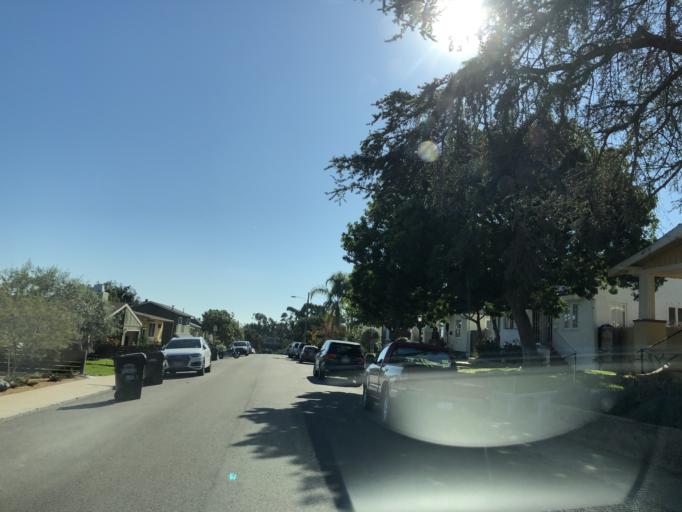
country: US
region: California
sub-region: San Diego County
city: San Diego
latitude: 32.7355
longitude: -117.1304
